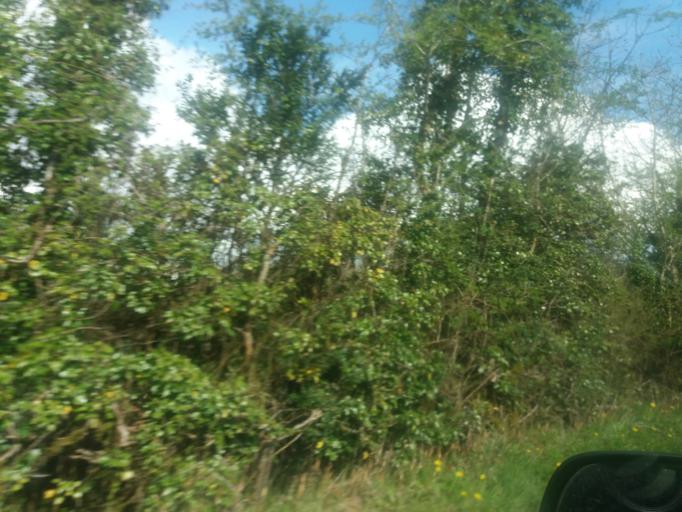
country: IE
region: Ulster
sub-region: An Cabhan
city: Belturbet
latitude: 54.1666
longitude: -7.5093
